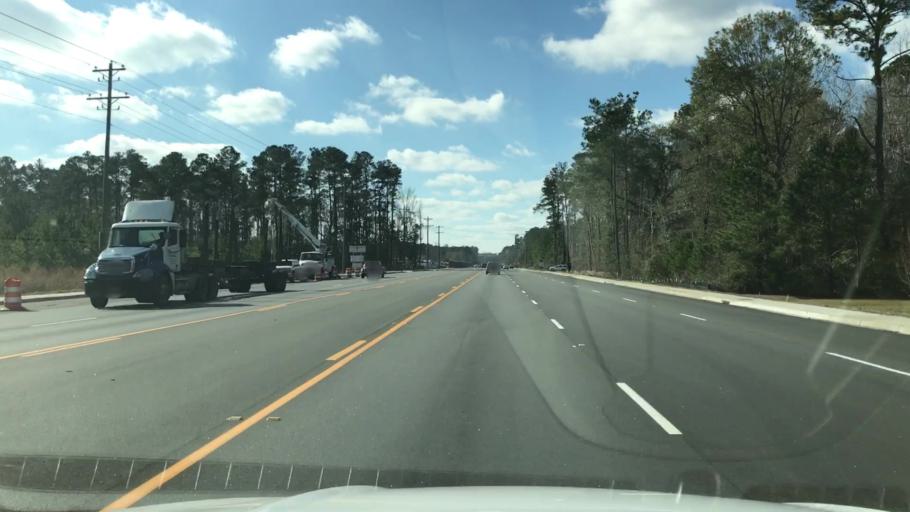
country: US
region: South Carolina
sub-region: Horry County
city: Socastee
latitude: 33.6491
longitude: -79.0231
